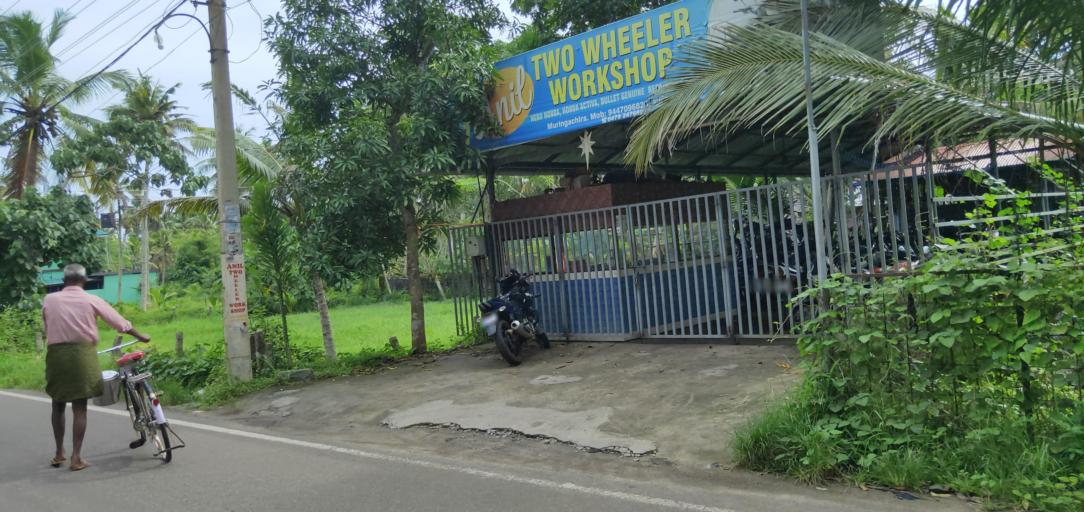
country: IN
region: Kerala
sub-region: Alappuzha
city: Kayankulam
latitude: 9.2277
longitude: 76.4584
